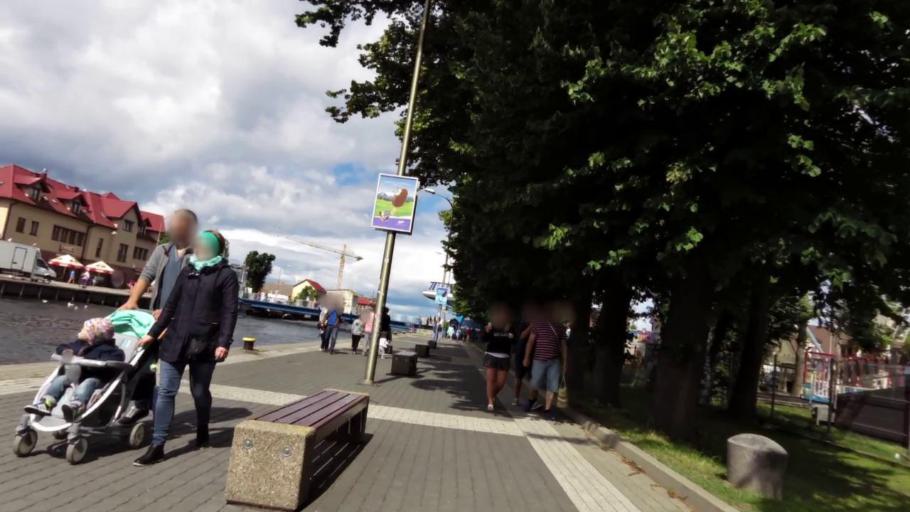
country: PL
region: West Pomeranian Voivodeship
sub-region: Powiat slawienski
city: Darlowo
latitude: 54.4391
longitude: 16.3815
